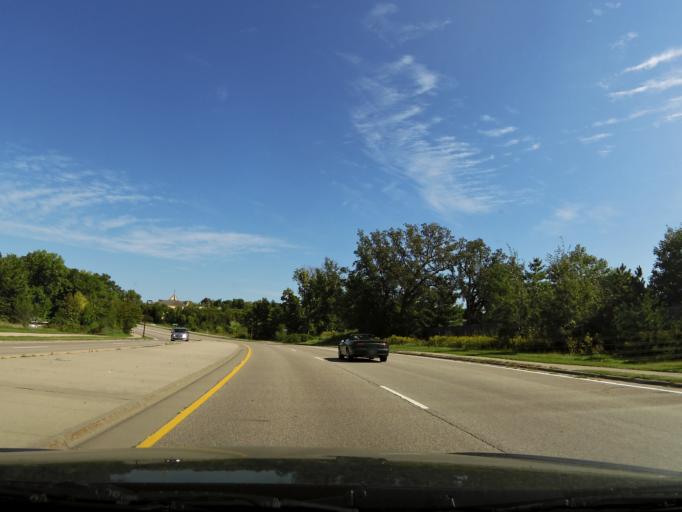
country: US
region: Minnesota
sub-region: Carver County
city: Chanhassen
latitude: 44.8501
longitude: -93.5352
